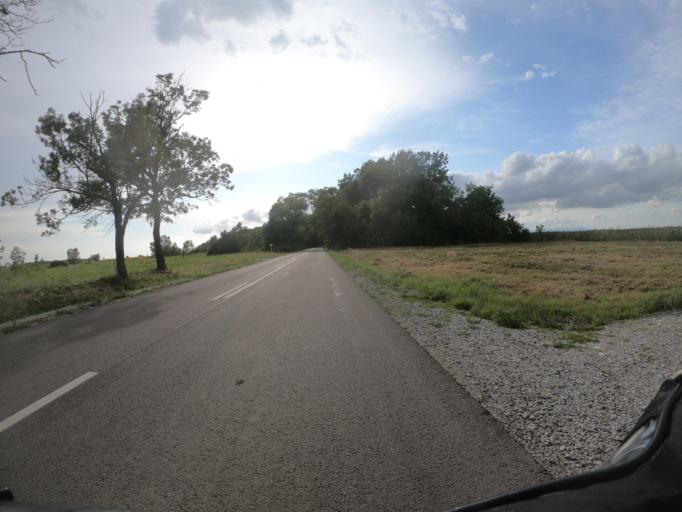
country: HU
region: Borsod-Abauj-Zemplen
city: Mezocsat
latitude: 47.8274
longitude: 20.8456
